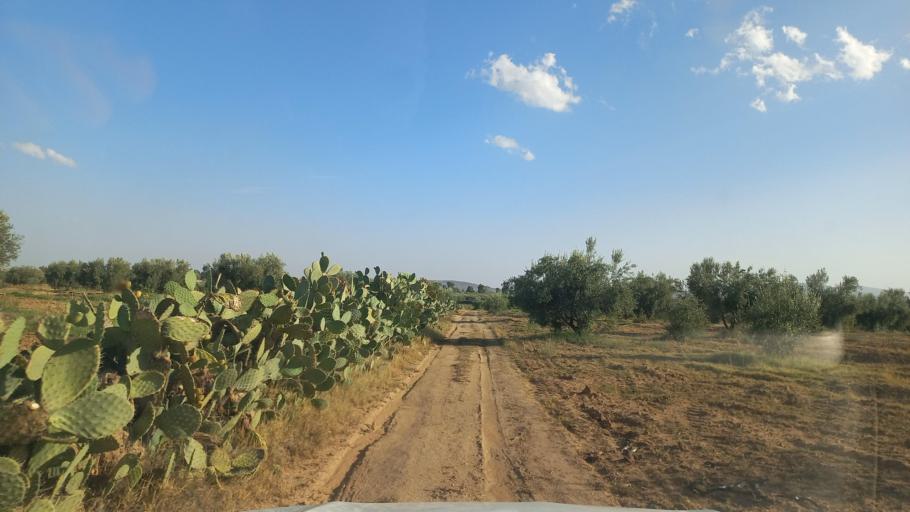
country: TN
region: Al Qasrayn
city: Kasserine
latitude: 35.2674
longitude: 9.0327
